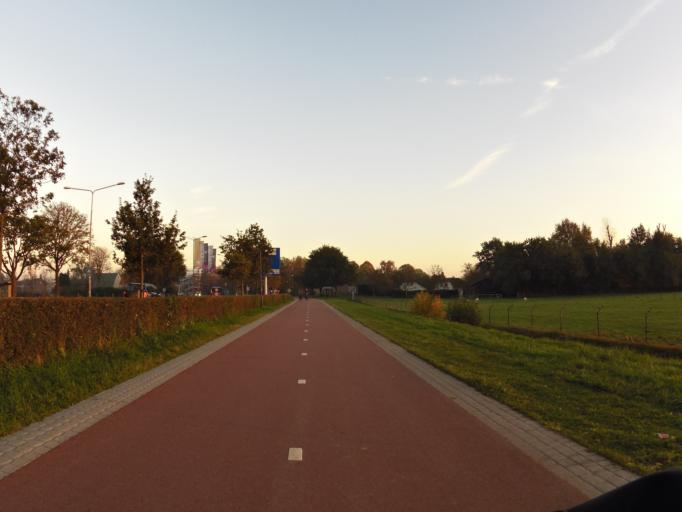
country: NL
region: North Brabant
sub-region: Gemeente 's-Hertogenbosch
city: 's-Hertogenbosch
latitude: 51.6881
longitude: 5.2685
